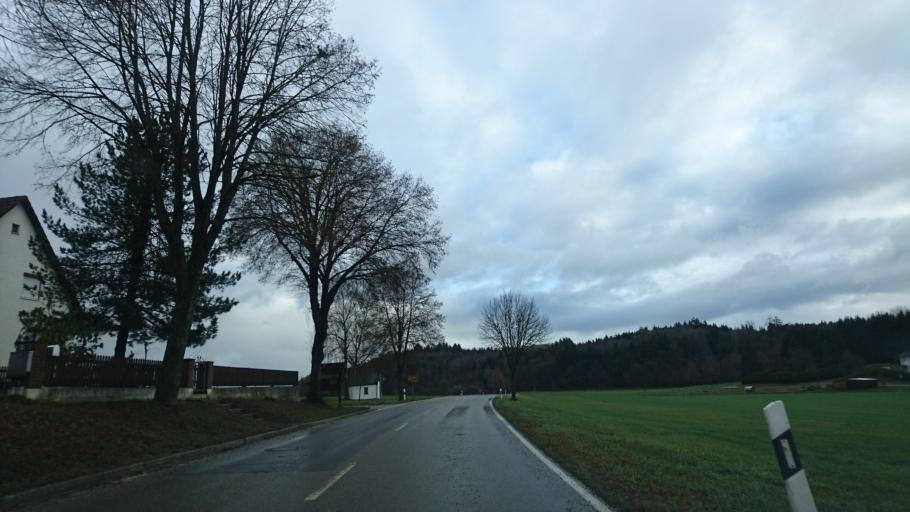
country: DE
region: Bavaria
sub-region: Swabia
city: Heretsried
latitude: 48.4746
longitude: 10.7175
